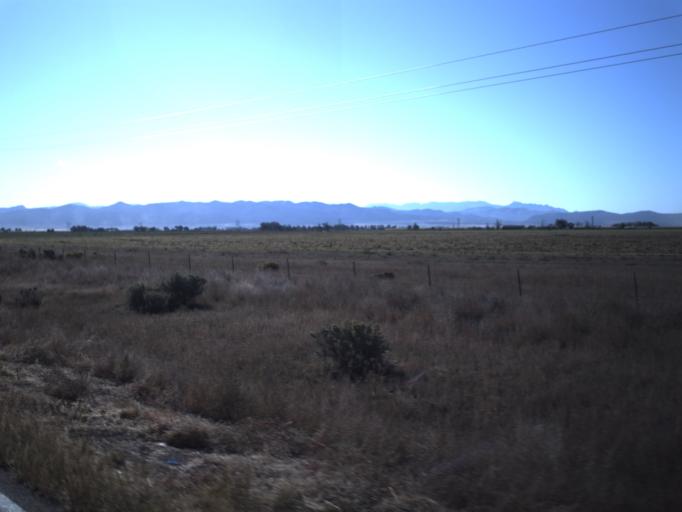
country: US
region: Utah
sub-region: Washington County
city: Enterprise
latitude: 37.7175
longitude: -113.6786
